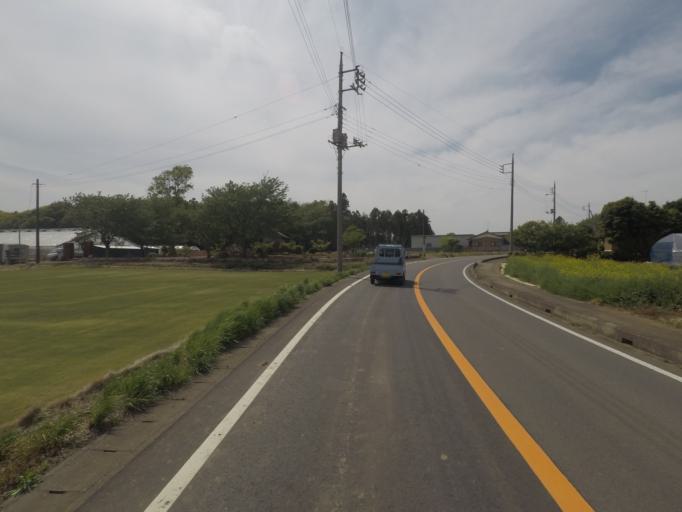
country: JP
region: Ibaraki
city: Ishige
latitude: 36.0950
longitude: 140.0259
